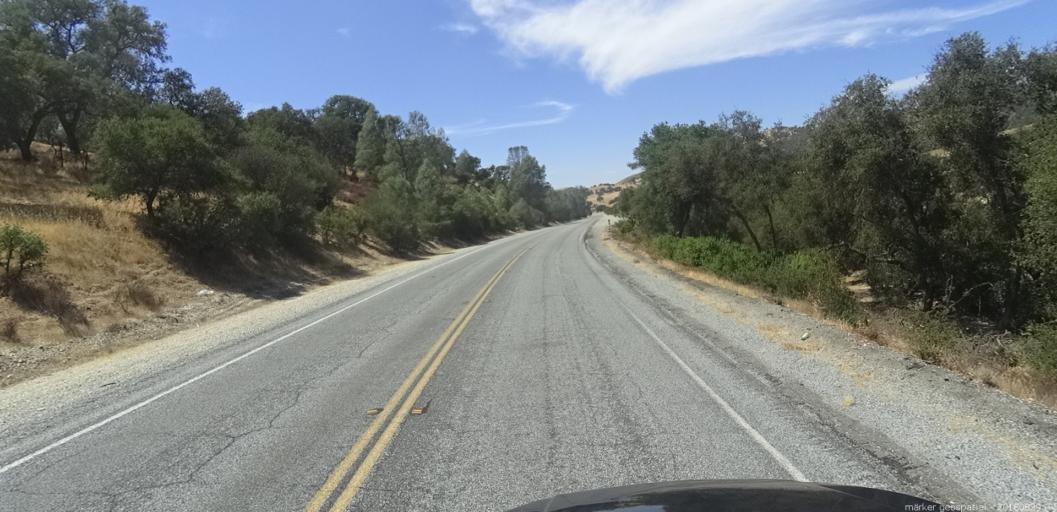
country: US
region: California
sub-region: San Luis Obispo County
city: Lake Nacimiento
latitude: 35.9028
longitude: -120.9744
